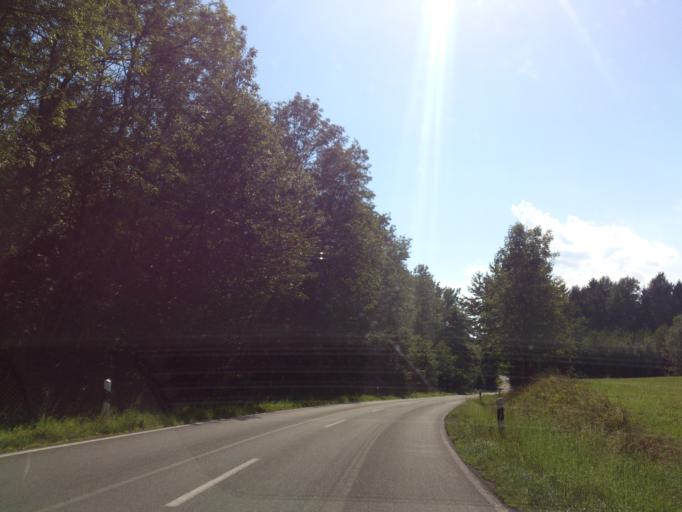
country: DE
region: North Rhine-Westphalia
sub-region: Regierungsbezirk Detmold
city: Willebadessen
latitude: 51.6449
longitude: 9.0452
